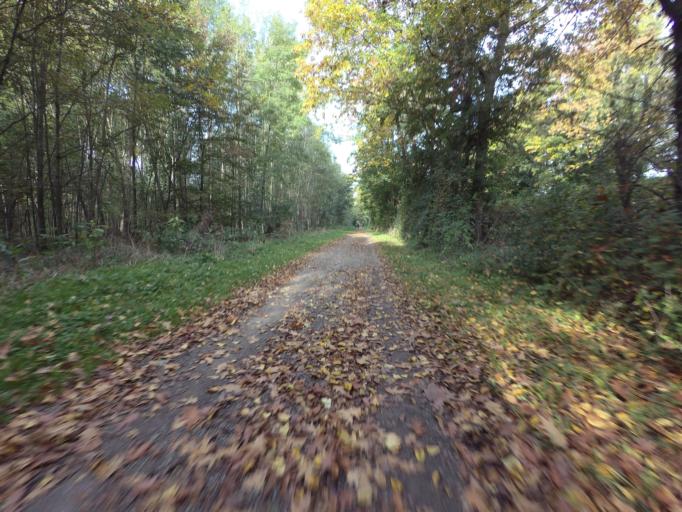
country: DE
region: North Rhine-Westphalia
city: Julich
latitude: 50.9449
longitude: 6.3349
